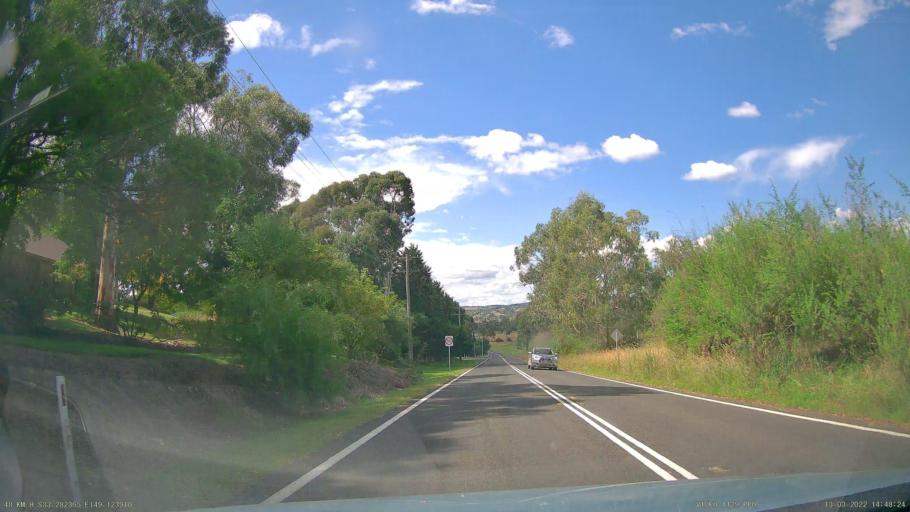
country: AU
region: New South Wales
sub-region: Orange Municipality
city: Orange
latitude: -33.2823
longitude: 149.1240
